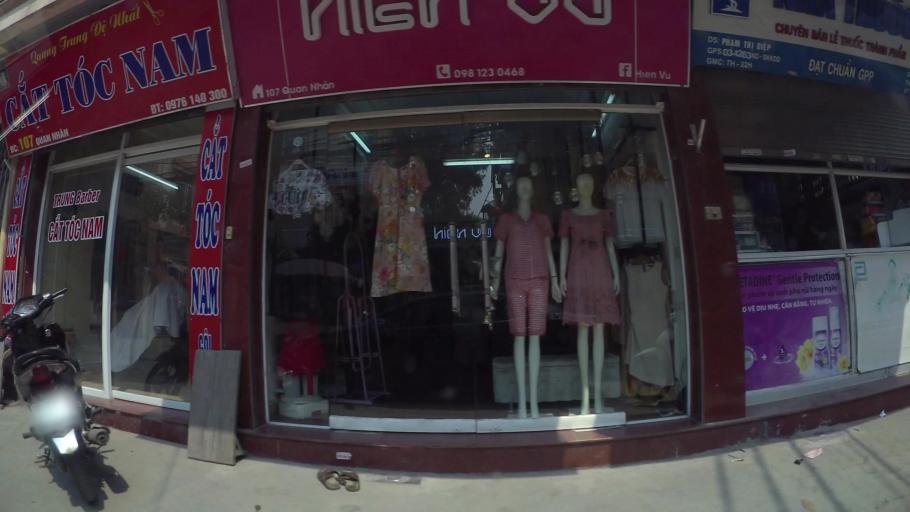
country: VN
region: Ha Noi
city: Thanh Xuan
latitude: 21.0053
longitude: 105.8116
